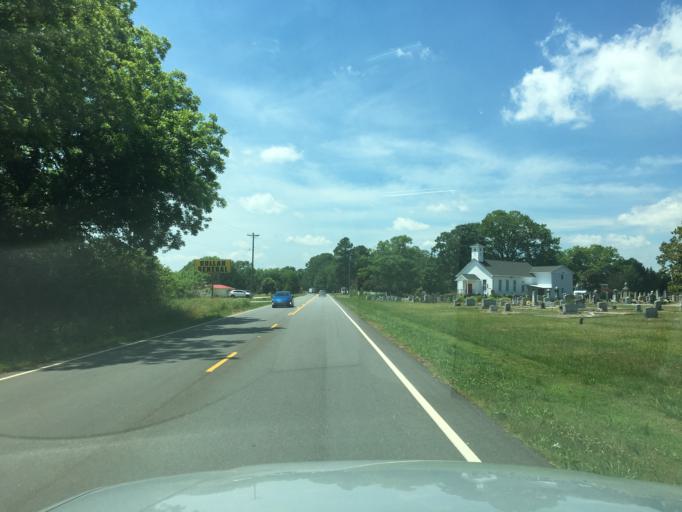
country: US
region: Georgia
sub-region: Hart County
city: Reed Creek
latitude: 34.5115
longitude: -82.9792
